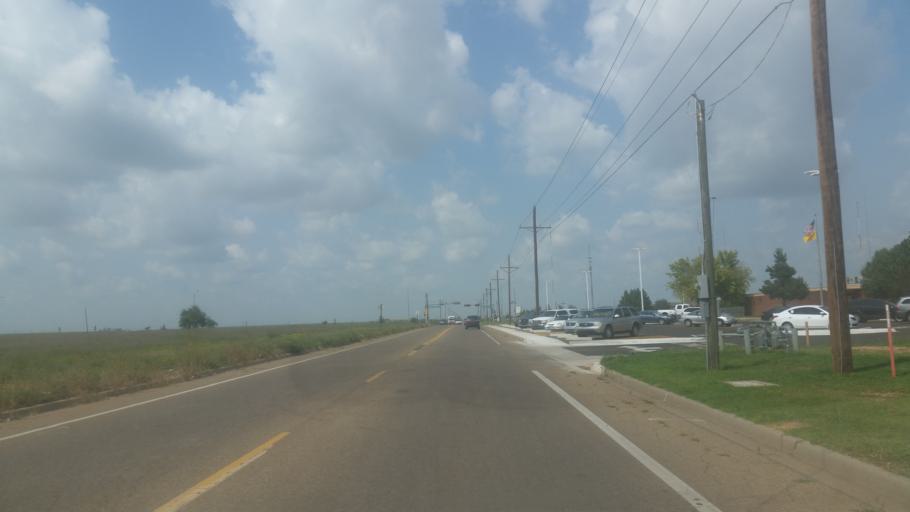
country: US
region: New Mexico
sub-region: Curry County
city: Clovis
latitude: 34.4320
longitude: -103.2141
